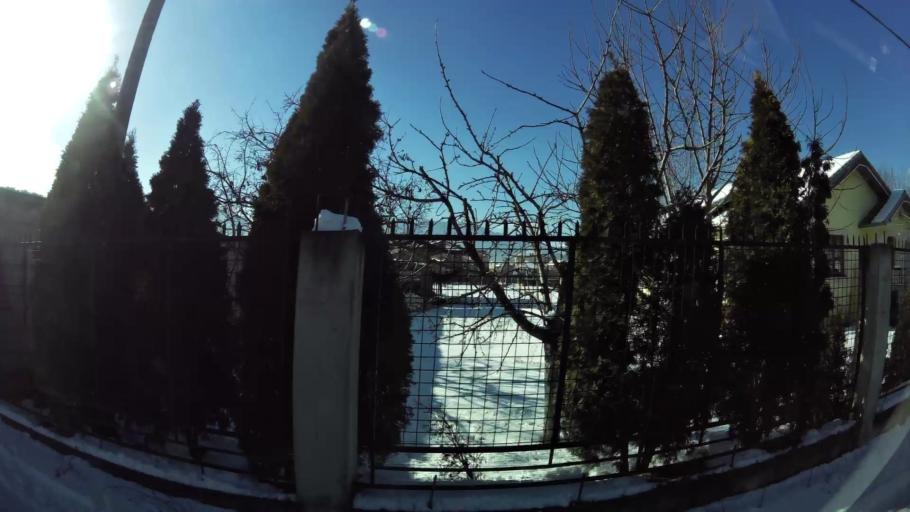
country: MK
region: Saraj
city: Saraj
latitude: 42.0018
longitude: 21.3283
